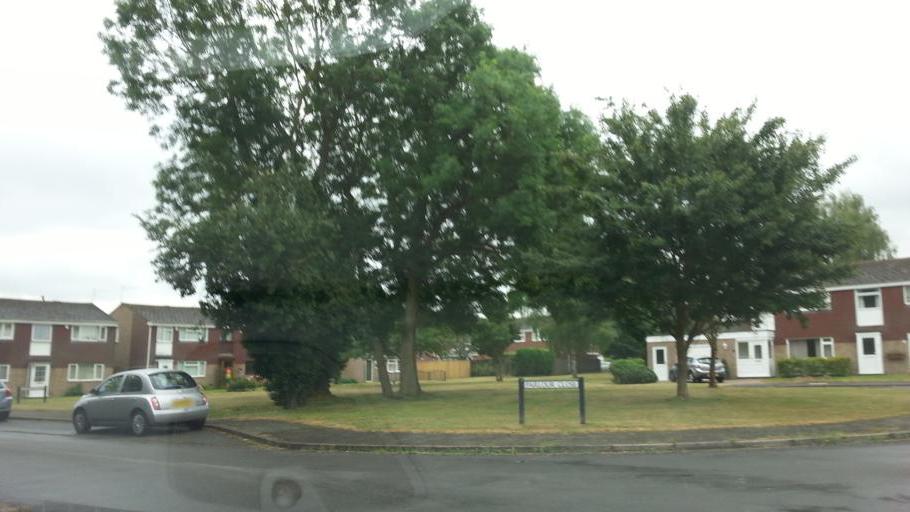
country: GB
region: England
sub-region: Cambridgeshire
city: Histon
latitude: 52.2576
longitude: 0.1068
